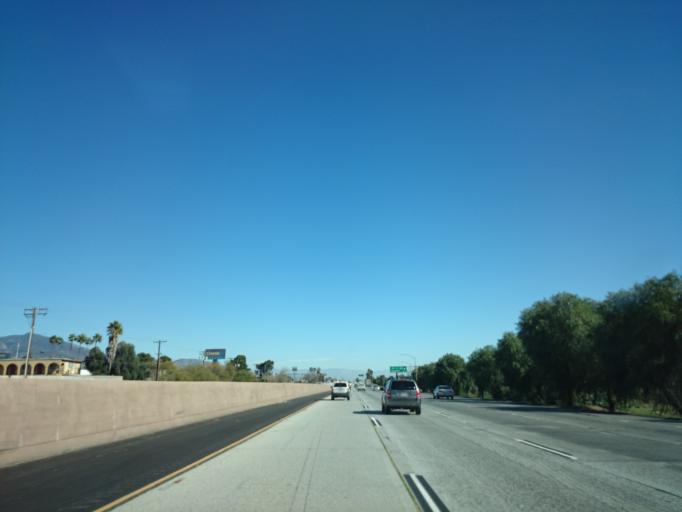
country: US
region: California
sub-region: Riverside County
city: Banning
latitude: 33.9241
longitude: -116.8910
